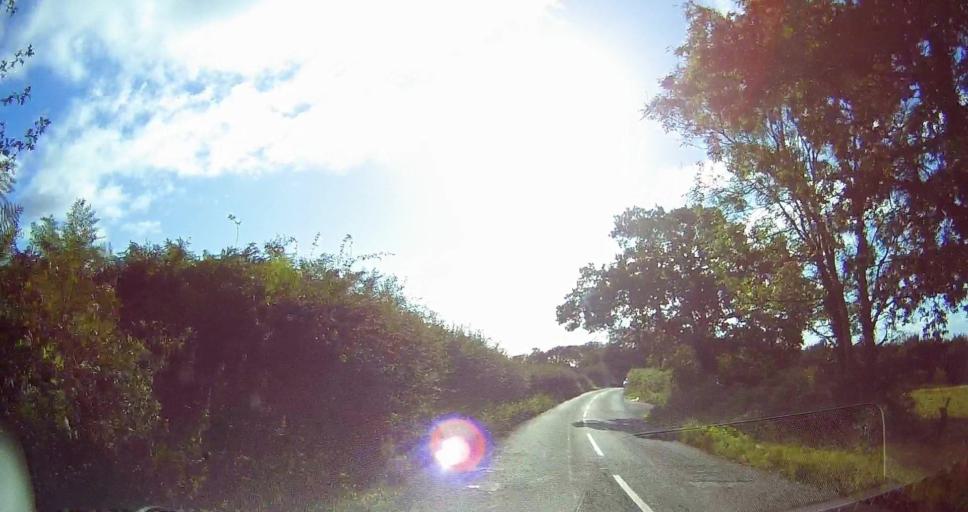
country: GB
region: England
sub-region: Kent
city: Borough Green
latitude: 51.3172
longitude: 0.2791
